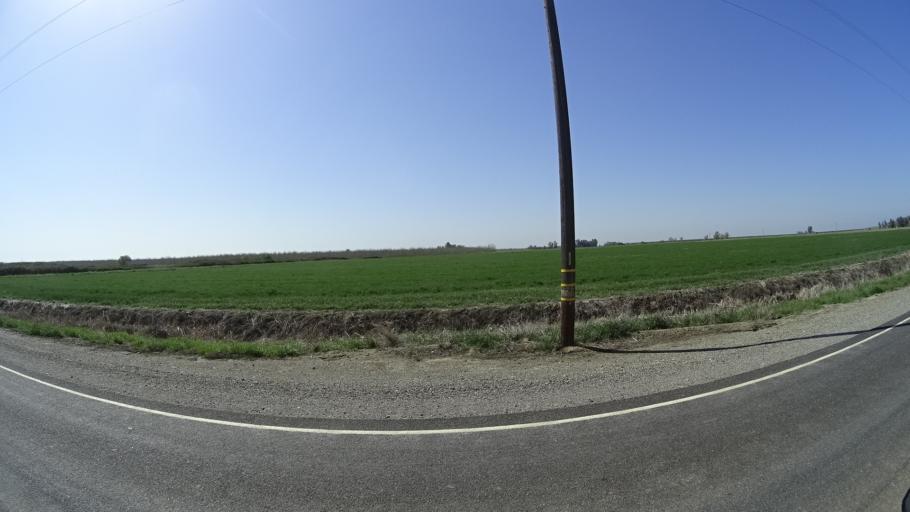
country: US
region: California
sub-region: Glenn County
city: Hamilton City
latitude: 39.6597
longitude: -122.0359
